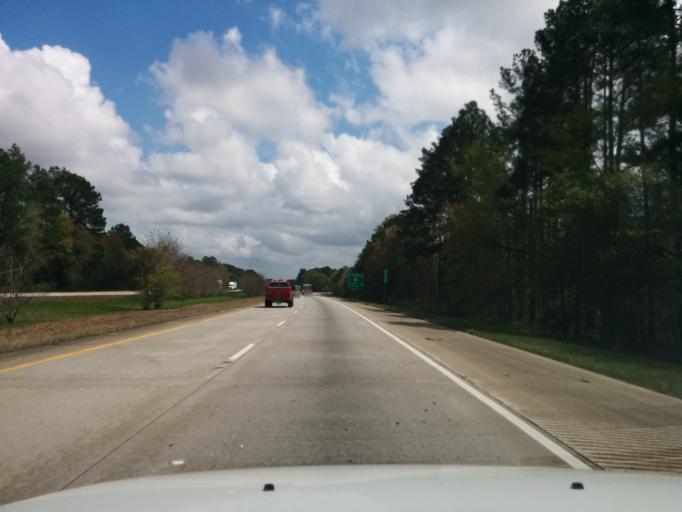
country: US
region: Georgia
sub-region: Bulloch County
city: Brooklet
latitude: 32.2571
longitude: -81.7200
